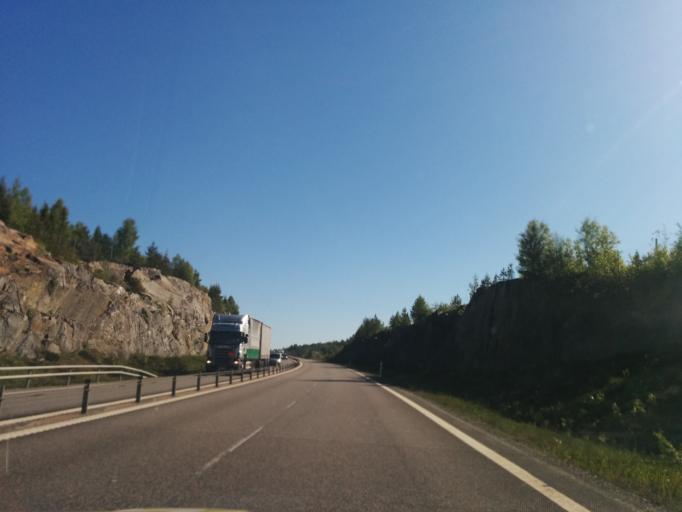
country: SE
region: Vaesternorrland
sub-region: Haernoesands Kommun
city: Haernoesand
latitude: 62.7142
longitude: 17.9056
